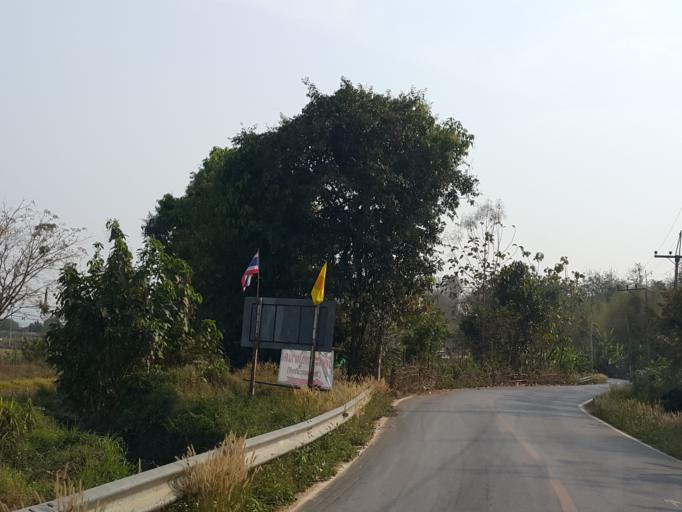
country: TH
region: Lampang
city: Chae Hom
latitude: 18.7238
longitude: 99.5618
